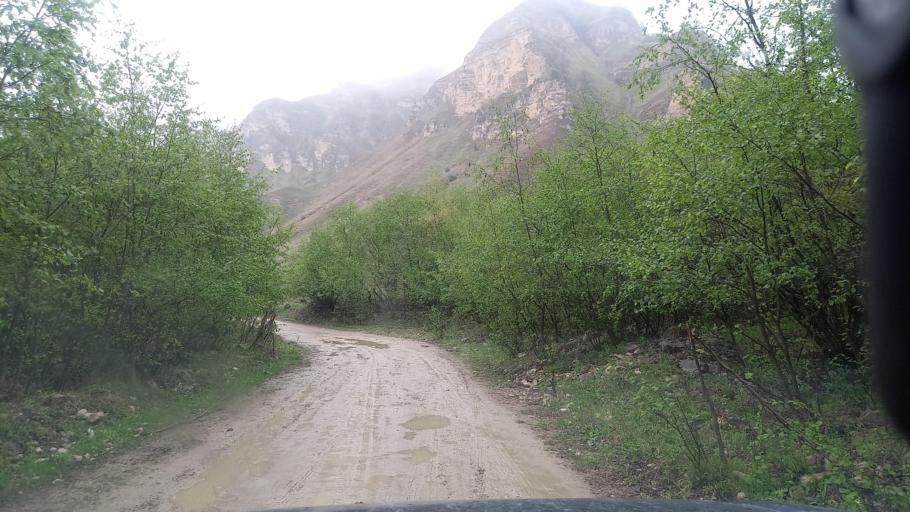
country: RU
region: Kabardino-Balkariya
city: Gundelen
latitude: 43.5977
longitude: 43.0485
